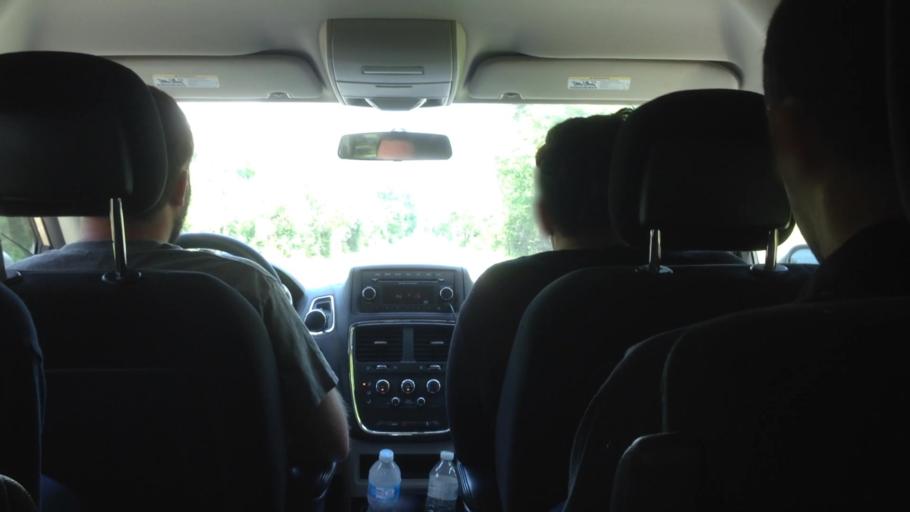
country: US
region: New York
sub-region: Dutchess County
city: Tivoli
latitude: 42.1076
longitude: -73.8945
